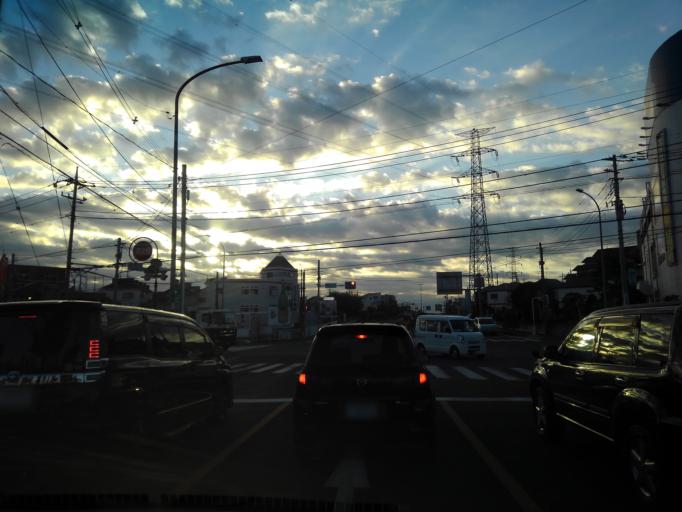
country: JP
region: Saitama
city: Tokorozawa
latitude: 35.7917
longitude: 139.4443
